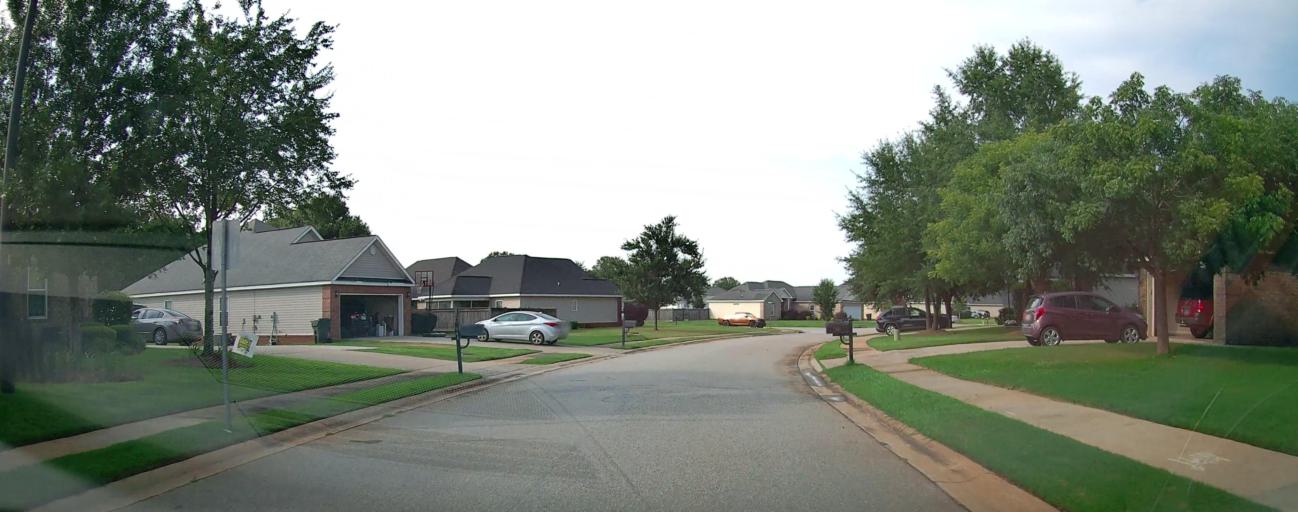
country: US
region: Georgia
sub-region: Houston County
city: Centerville
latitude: 32.6301
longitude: -83.7230
